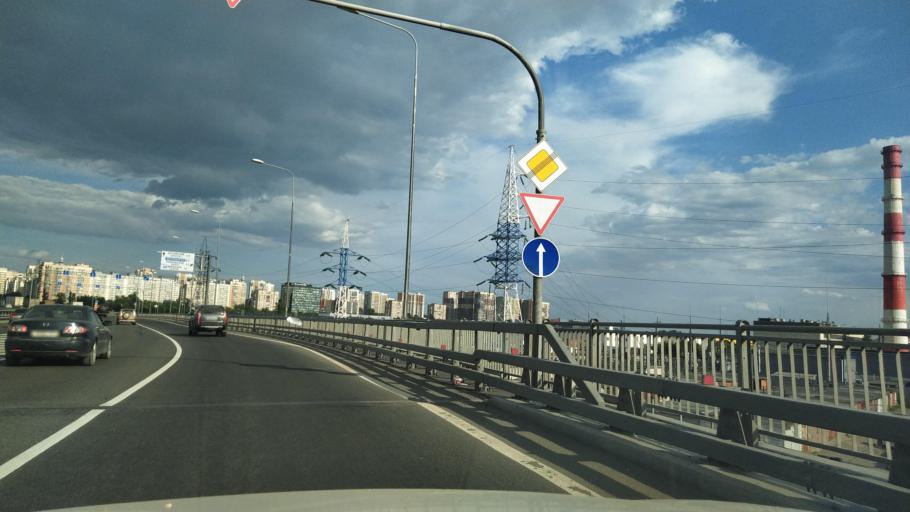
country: RU
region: St.-Petersburg
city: Kupchino
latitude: 59.8310
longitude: 30.3120
